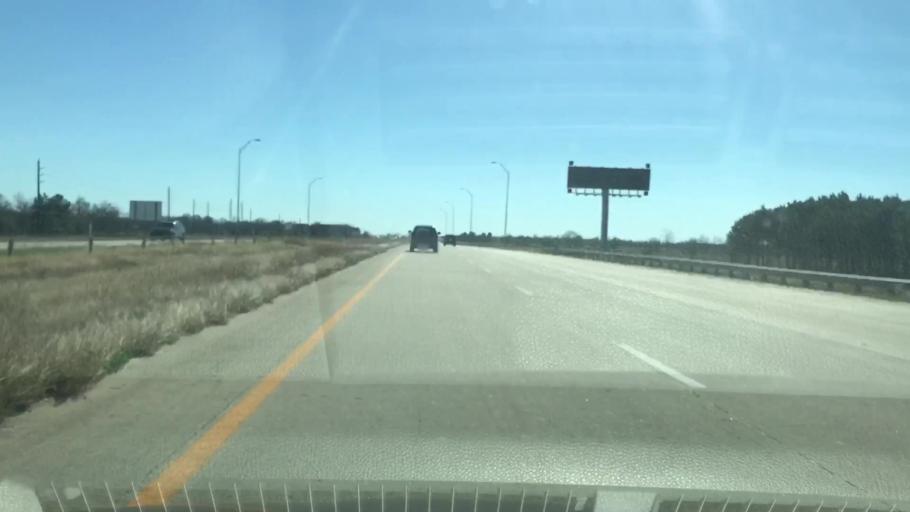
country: US
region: Texas
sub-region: Harris County
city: Cypress
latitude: 29.9001
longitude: -95.7584
